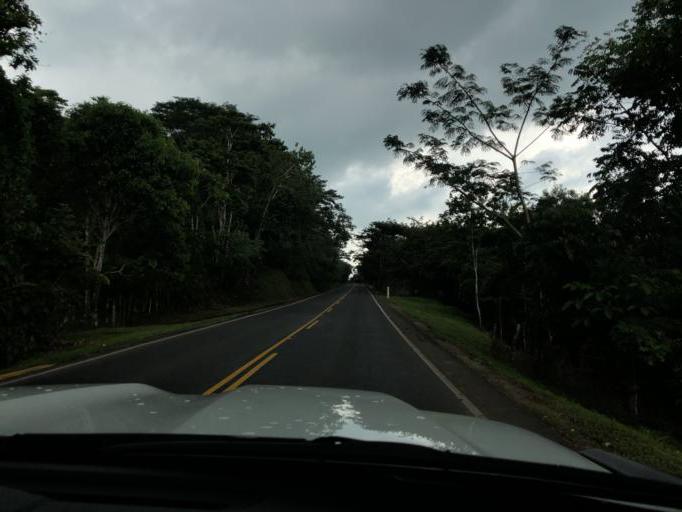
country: NI
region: Chontales
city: Villa Sandino
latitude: 11.9902
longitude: -84.8145
